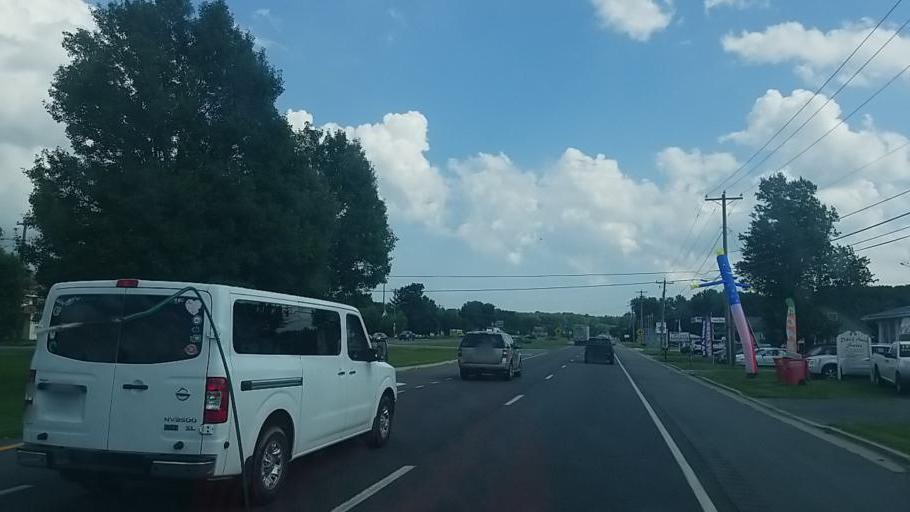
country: US
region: Delaware
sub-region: Sussex County
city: Selbyville
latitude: 38.5195
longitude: -75.2418
